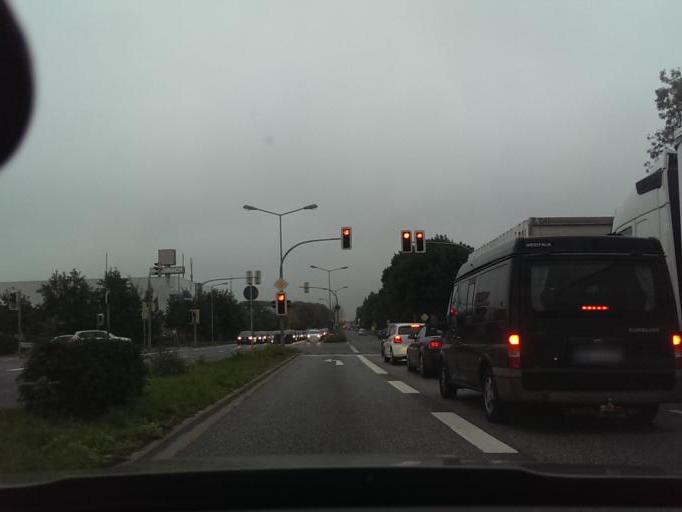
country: DE
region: Lower Saxony
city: Garbsen-Mitte
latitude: 52.4292
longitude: 9.6176
